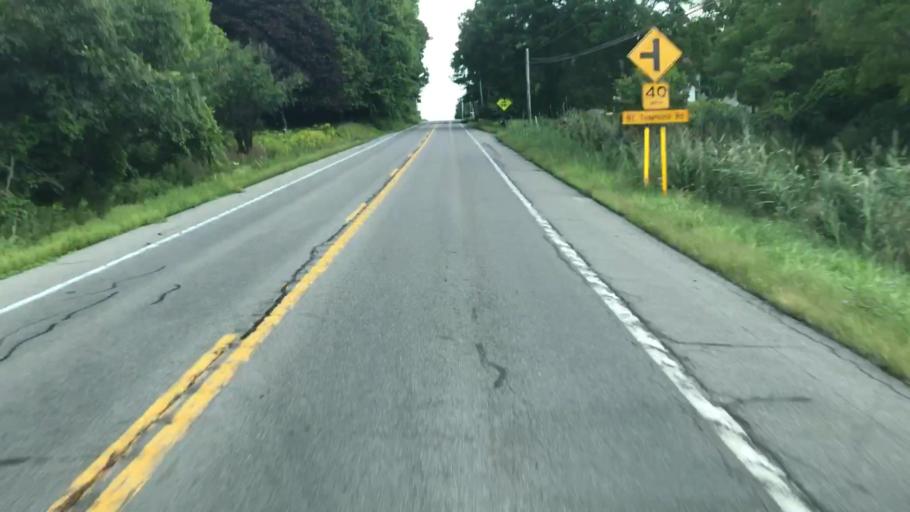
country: US
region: New York
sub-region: Onondaga County
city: Marcellus
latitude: 42.9840
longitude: -76.2904
